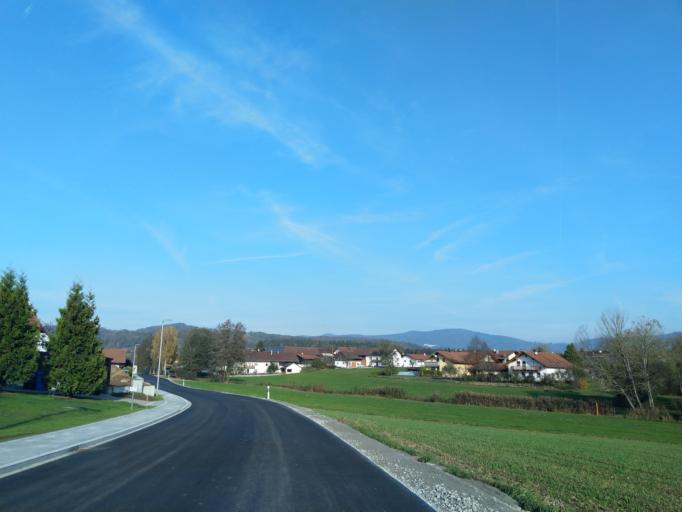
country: DE
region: Bavaria
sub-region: Lower Bavaria
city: Auerbach
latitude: 48.8041
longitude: 13.0924
